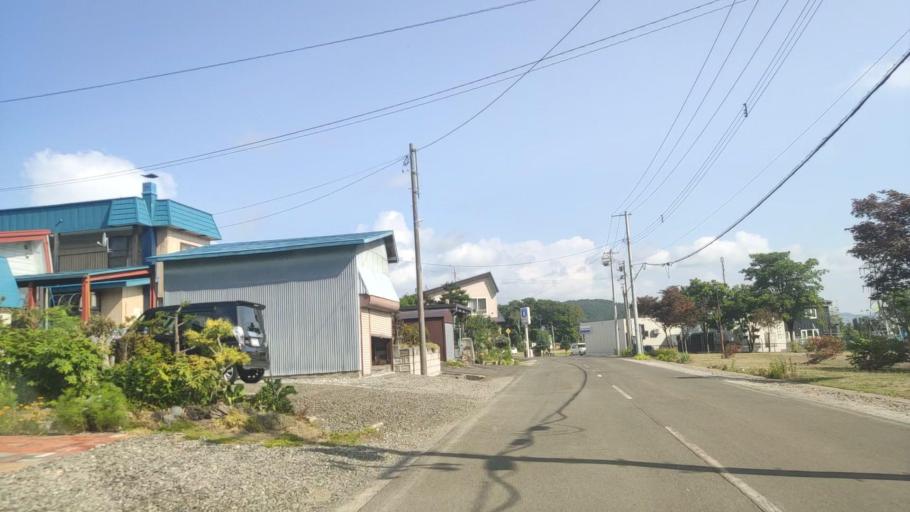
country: JP
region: Hokkaido
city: Shimo-furano
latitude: 43.3431
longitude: 142.3704
